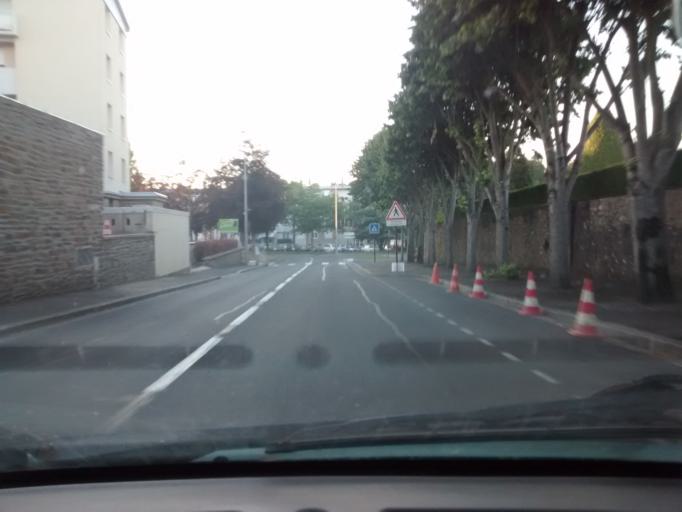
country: FR
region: Lower Normandy
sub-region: Departement de la Manche
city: Saint-Lo
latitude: 49.1174
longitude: -1.0831
